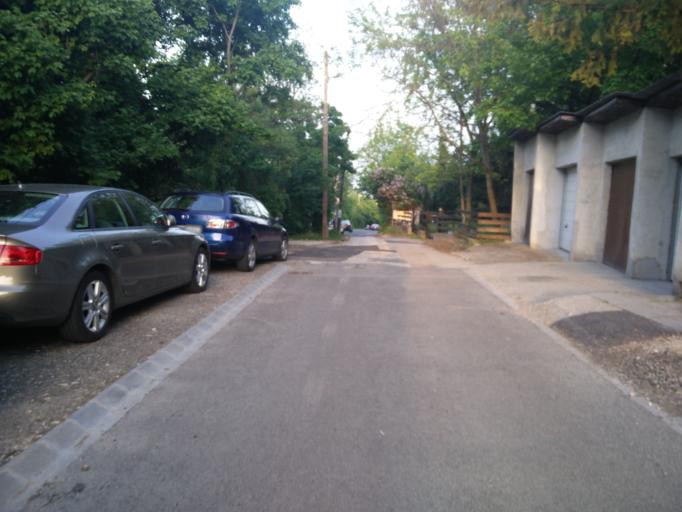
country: HU
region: Budapest
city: Budapest XII. keruelet
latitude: 47.5105
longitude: 18.9914
